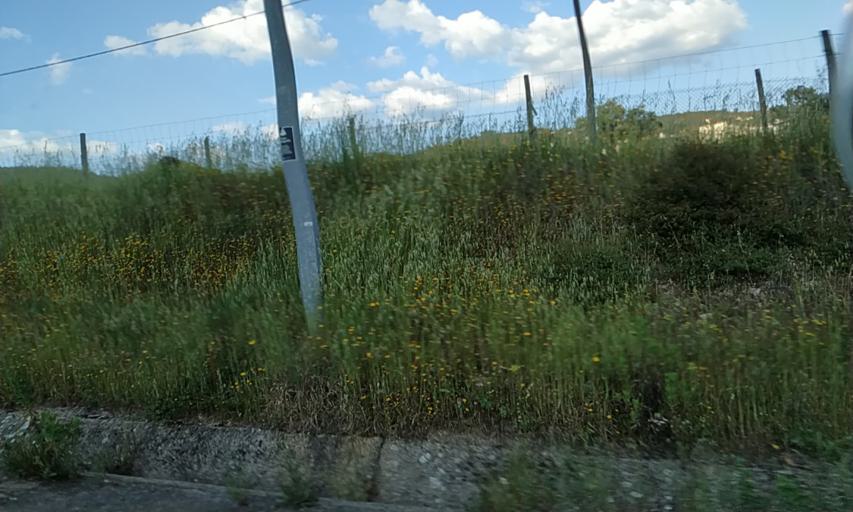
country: PT
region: Portalegre
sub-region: Portalegre
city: Portalegre
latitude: 39.3000
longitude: -7.4392
